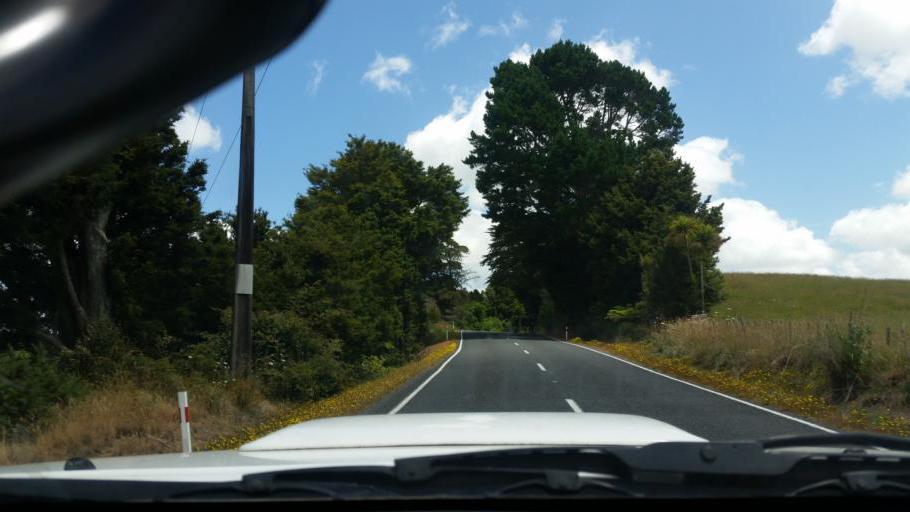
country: NZ
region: Northland
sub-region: Whangarei
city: Ruakaka
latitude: -36.0464
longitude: 174.2778
